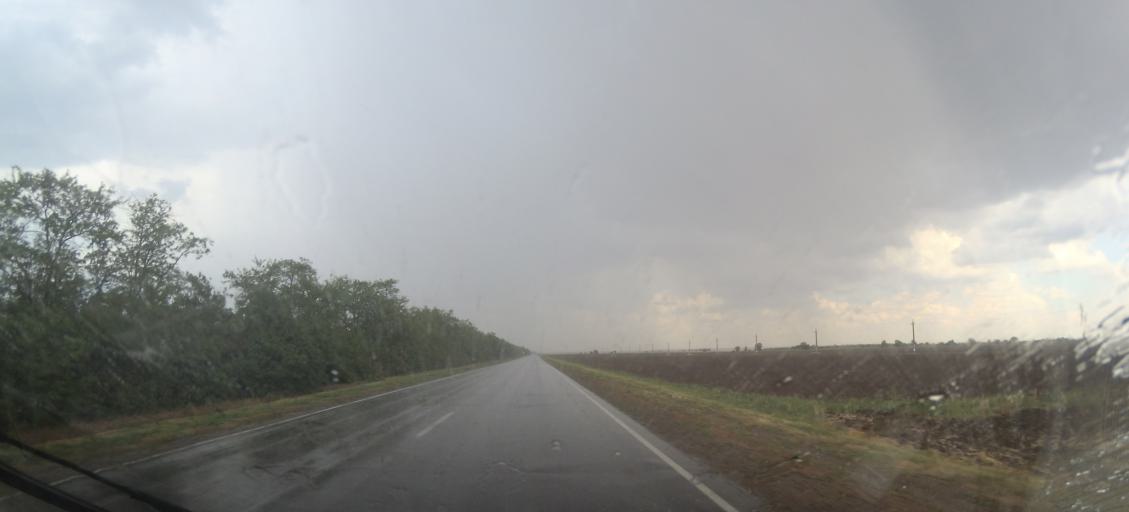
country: RU
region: Rostov
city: Proletarsk
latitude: 46.6524
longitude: 41.6789
